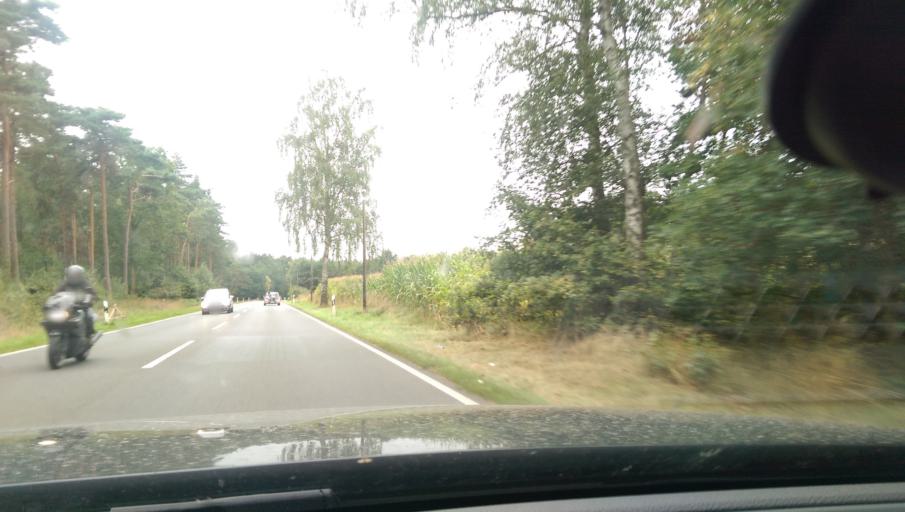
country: DE
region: Lower Saxony
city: Hagenburg
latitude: 52.4842
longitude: 9.2736
